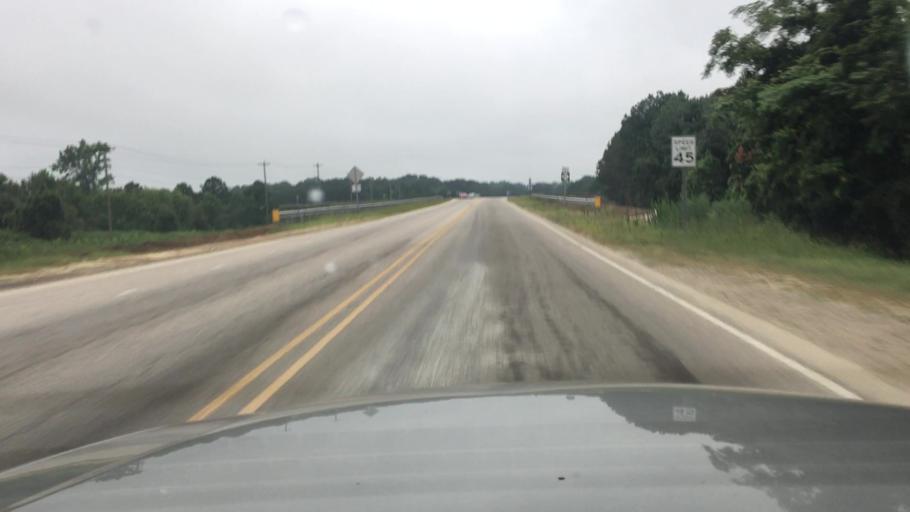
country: US
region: North Carolina
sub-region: Cumberland County
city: Fayetteville
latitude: 35.0104
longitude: -78.8647
